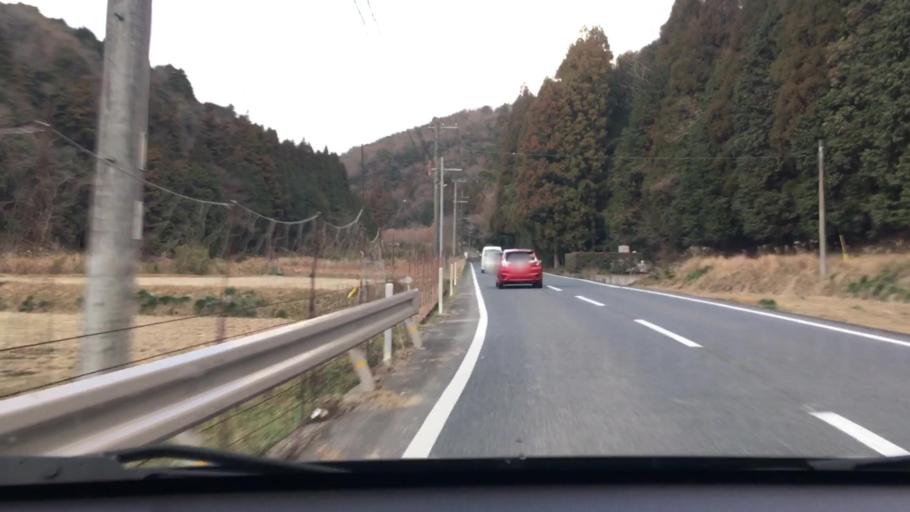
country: JP
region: Oita
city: Bungo-Takada-shi
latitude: 33.4533
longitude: 131.3926
